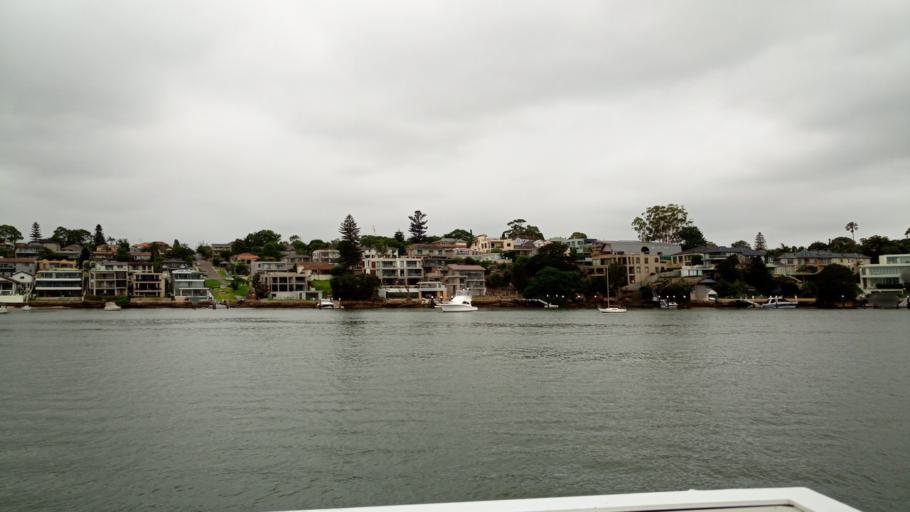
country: AU
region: New South Wales
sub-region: Hunters Hill
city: Gladesville
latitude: -33.8411
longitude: 151.1217
